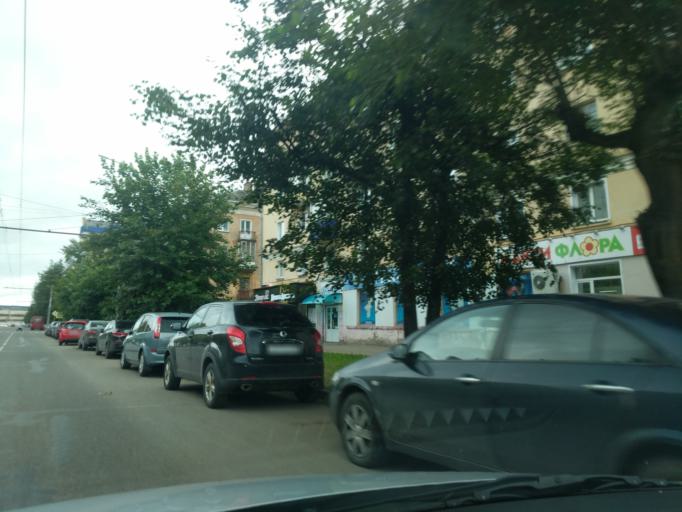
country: RU
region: Kirov
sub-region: Kirovo-Chepetskiy Rayon
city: Kirov
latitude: 58.6377
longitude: 49.6173
